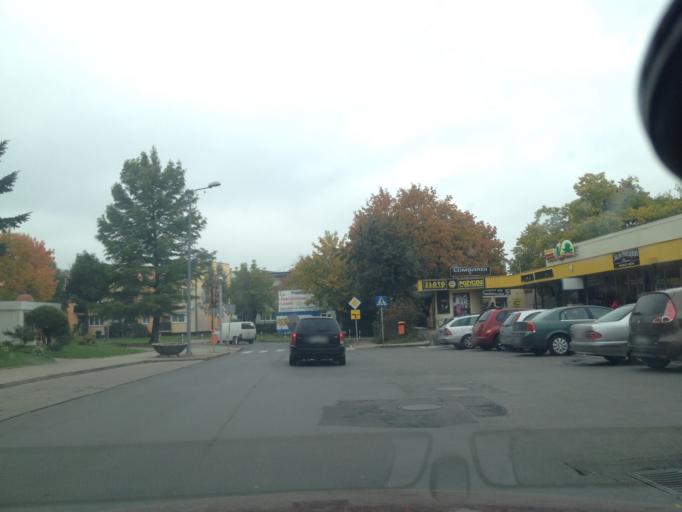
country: PL
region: Lower Silesian Voivodeship
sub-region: Powiat zgorzelecki
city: Zgorzelec
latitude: 51.1550
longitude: 15.0151
